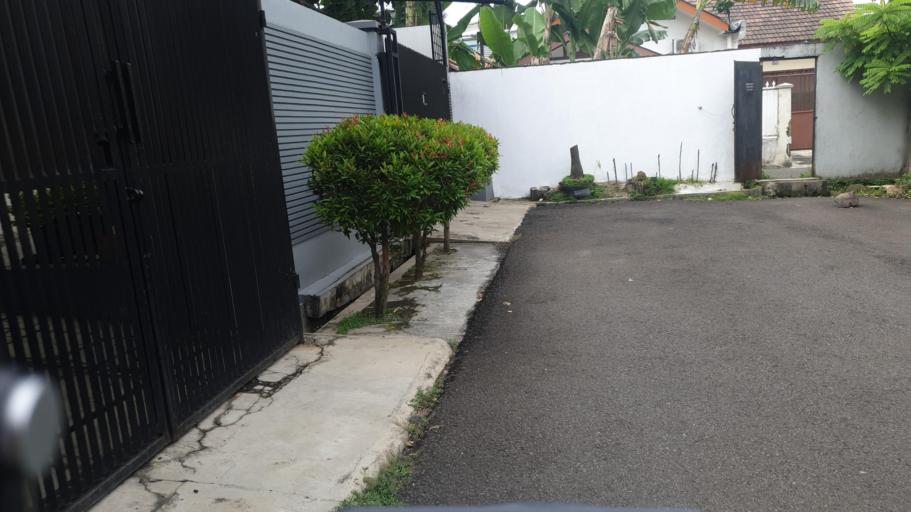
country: ID
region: West Java
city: Pamulang
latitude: -6.2945
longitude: 106.7927
